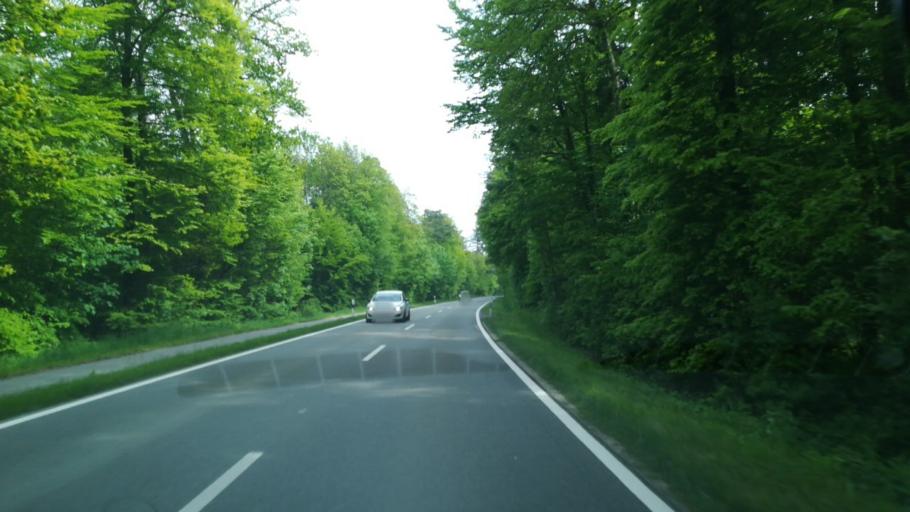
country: DE
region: Baden-Wuerttemberg
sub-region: Freiburg Region
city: Singen
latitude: 47.7701
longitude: 8.8848
